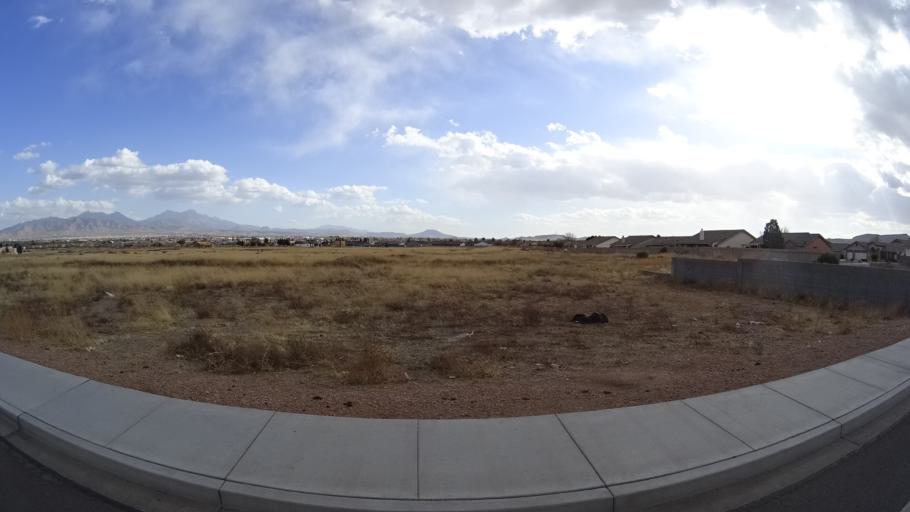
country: US
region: Arizona
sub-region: Mohave County
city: New Kingman-Butler
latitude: 35.2395
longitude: -114.0274
